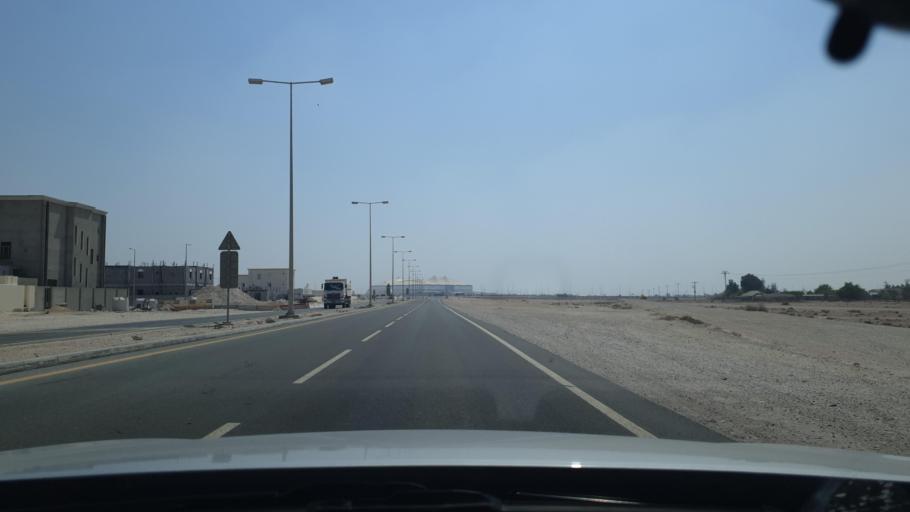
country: QA
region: Al Khawr
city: Al Khawr
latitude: 25.6719
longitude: 51.4708
